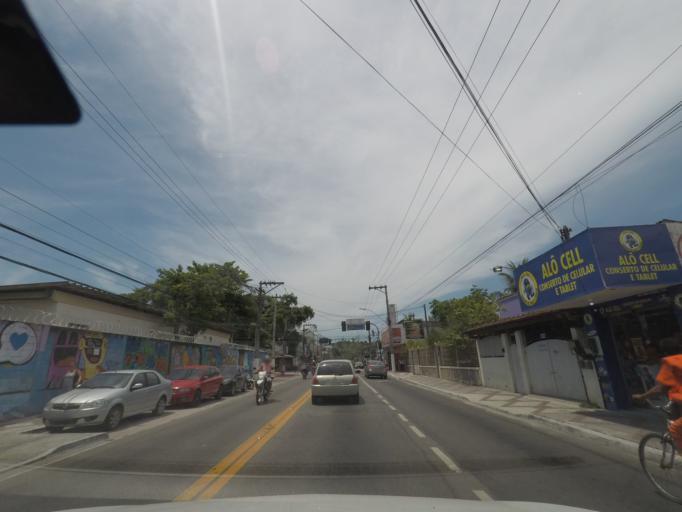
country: BR
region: Rio de Janeiro
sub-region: Marica
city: Marica
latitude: -22.9184
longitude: -42.8185
